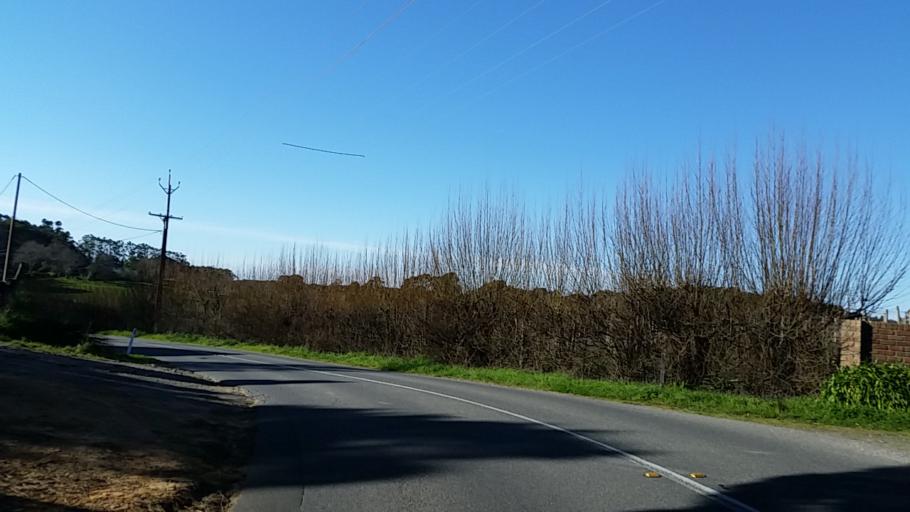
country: AU
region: South Australia
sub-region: Adelaide Hills
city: Adelaide Hills
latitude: -34.9523
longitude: 138.7219
